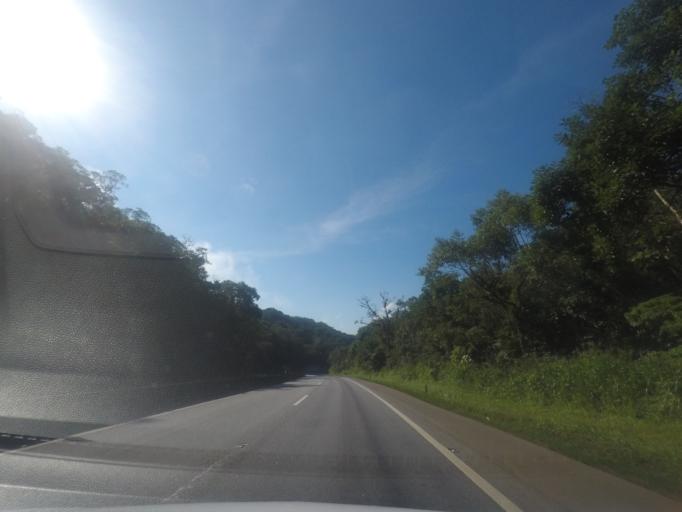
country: BR
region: Parana
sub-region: Piraquara
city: Piraquara
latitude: -25.5931
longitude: -48.9113
